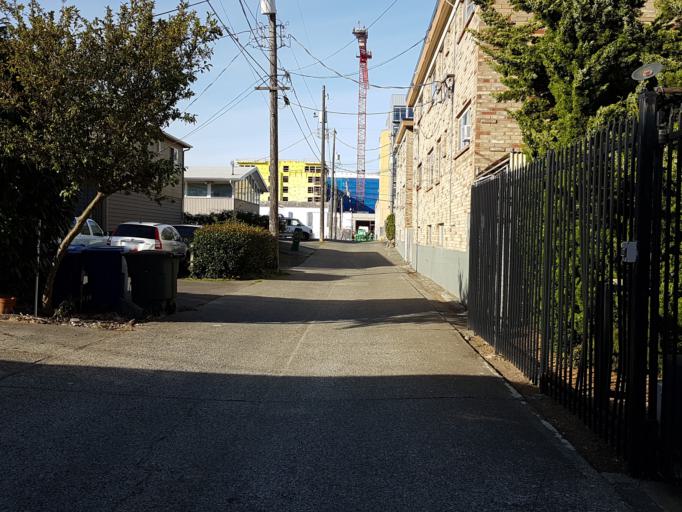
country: US
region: Washington
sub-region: King County
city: White Center
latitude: 47.5584
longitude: -122.3822
